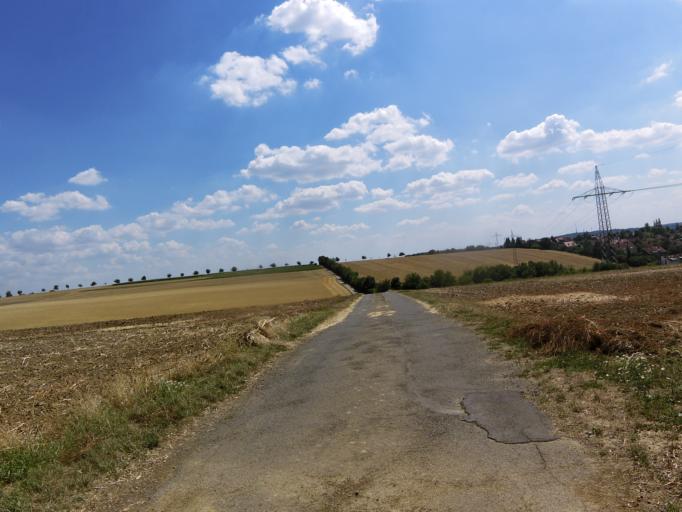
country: DE
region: Bavaria
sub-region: Regierungsbezirk Unterfranken
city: Gadheim
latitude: 49.8262
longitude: 9.9327
